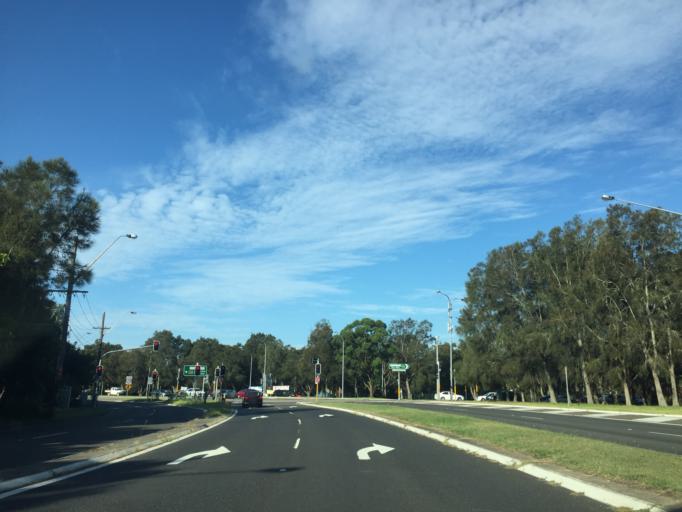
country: AU
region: New South Wales
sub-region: Pittwater
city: North Narrabeen
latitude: -33.7103
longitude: 151.2949
